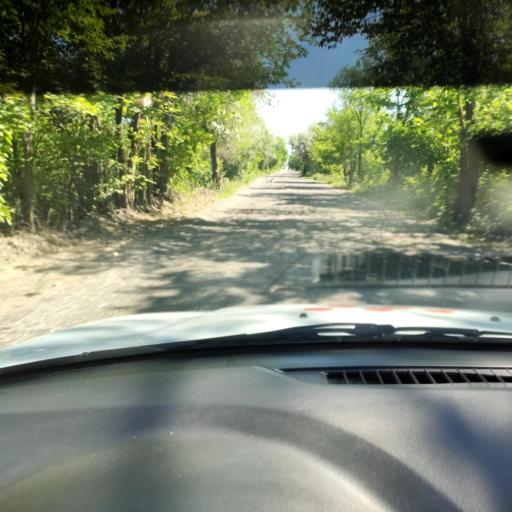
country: RU
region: Samara
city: Tol'yatti
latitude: 53.5649
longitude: 49.3648
